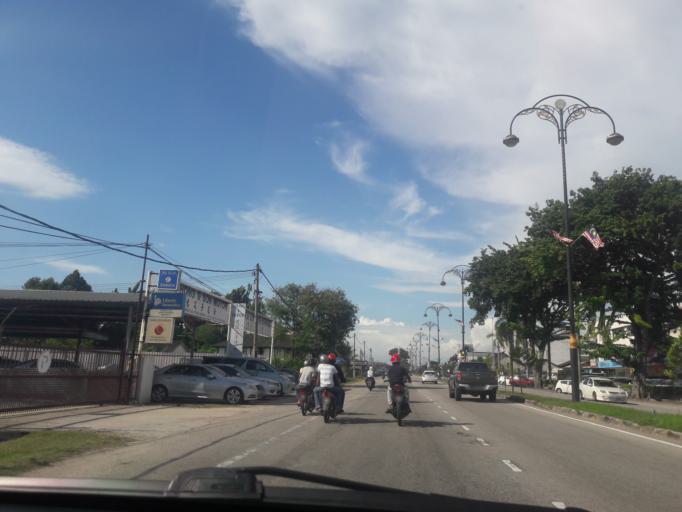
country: MY
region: Kedah
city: Sungai Petani
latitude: 5.6263
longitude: 100.4794
